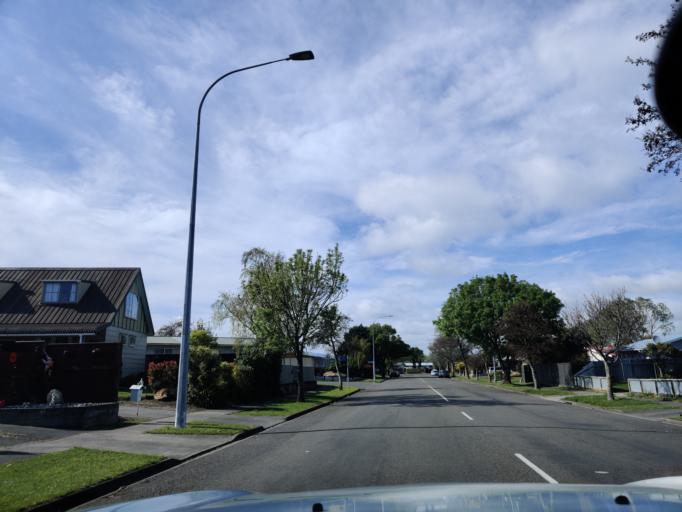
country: NZ
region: Manawatu-Wanganui
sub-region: Palmerston North City
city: Palmerston North
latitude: -40.3308
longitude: 175.6402
